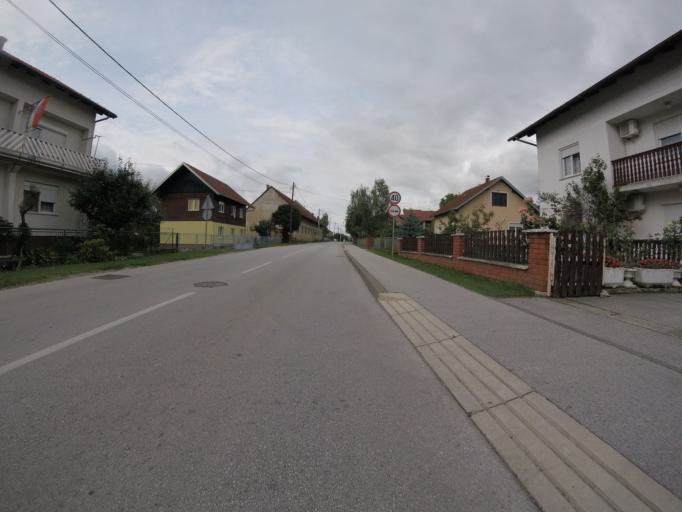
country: HR
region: Zagrebacka
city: Gradici
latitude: 45.7060
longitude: 16.0397
